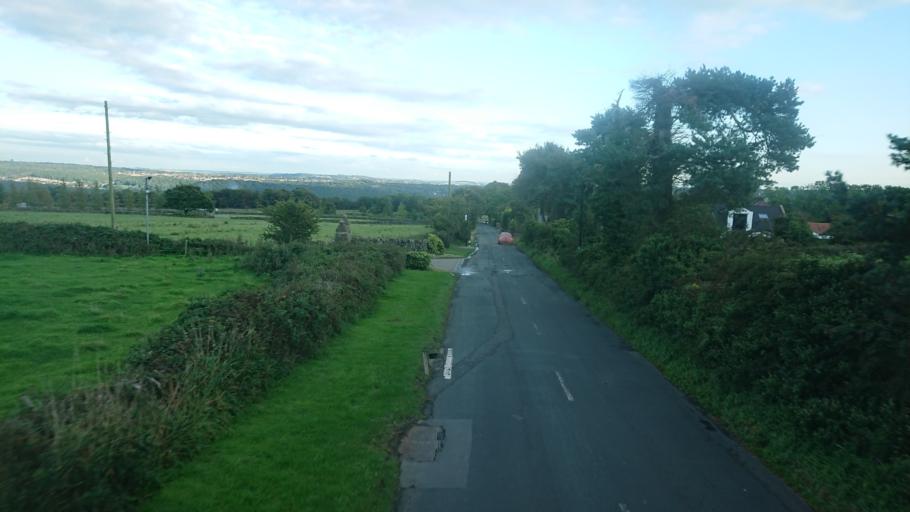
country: GB
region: England
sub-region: Derbyshire
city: Dronfield
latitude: 53.3375
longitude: -1.5494
